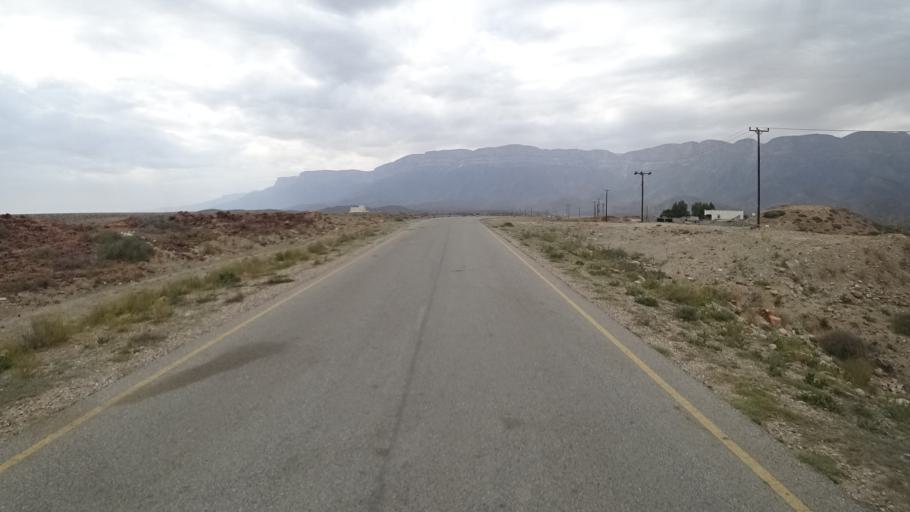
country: OM
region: Zufar
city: Salalah
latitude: 17.1530
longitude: 55.0051
